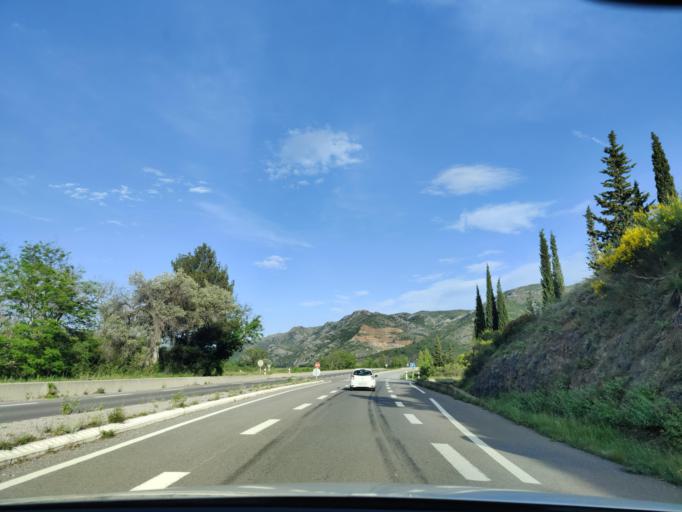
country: FR
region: Languedoc-Roussillon
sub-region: Departement des Pyrenees-Orientales
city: Estagel
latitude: 42.7756
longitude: 2.7384
